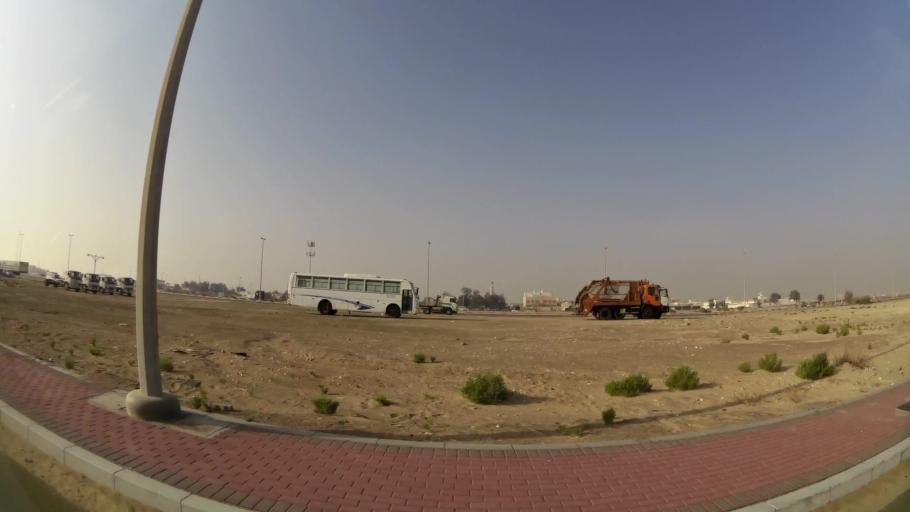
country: AE
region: Abu Dhabi
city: Abu Dhabi
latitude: 24.2741
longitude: 54.6459
